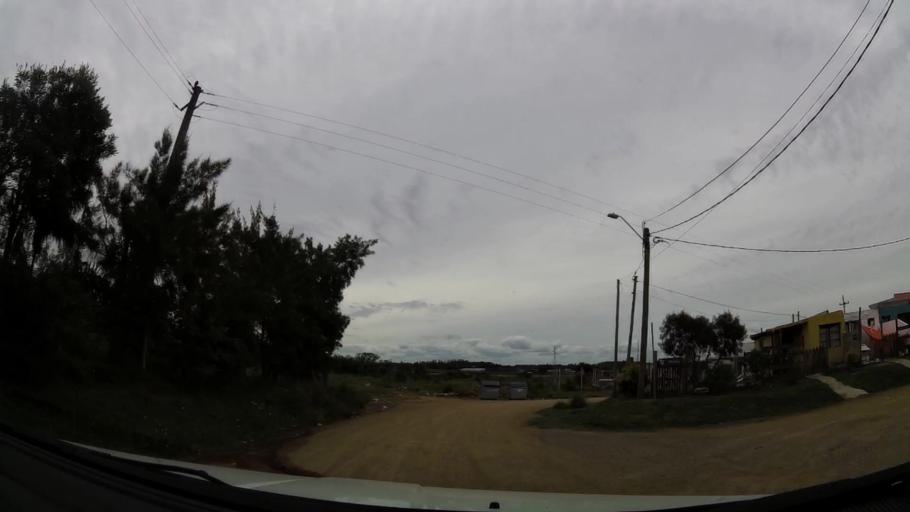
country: UY
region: Maldonado
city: Maldonado
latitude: -34.8834
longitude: -54.9419
